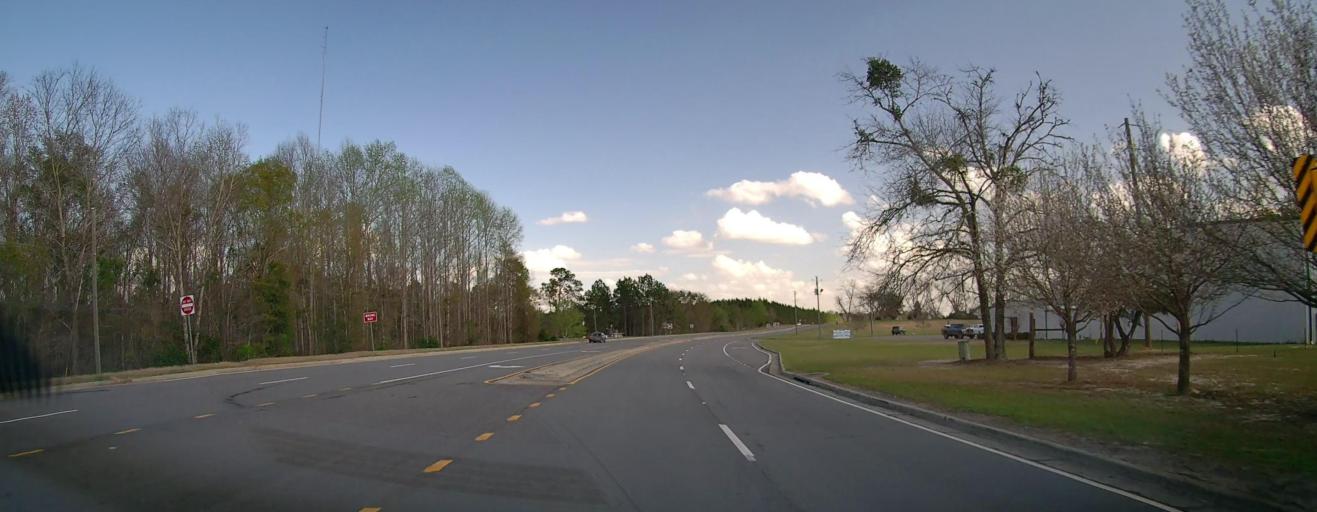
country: US
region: Georgia
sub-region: Telfair County
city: McRae
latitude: 32.0572
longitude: -82.8674
